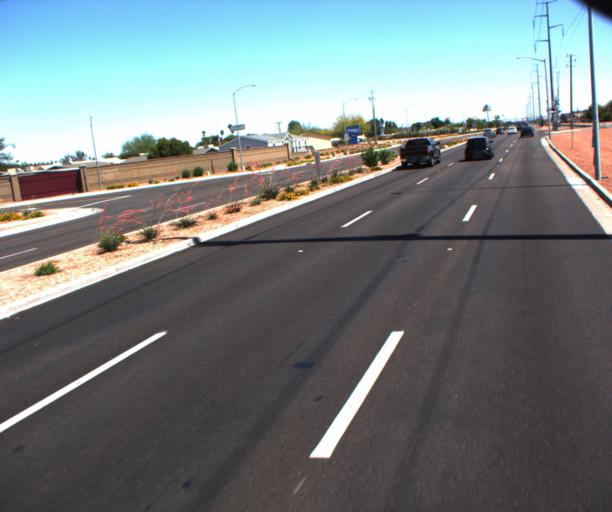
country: US
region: Arizona
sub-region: Maricopa County
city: Glendale
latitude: 33.5465
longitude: -112.1955
